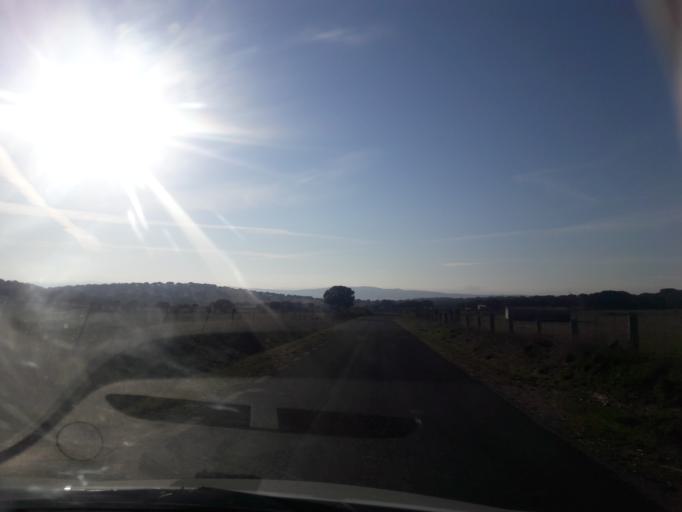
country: ES
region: Castille and Leon
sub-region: Provincia de Salamanca
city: Montejo
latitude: 40.6246
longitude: -5.6121
